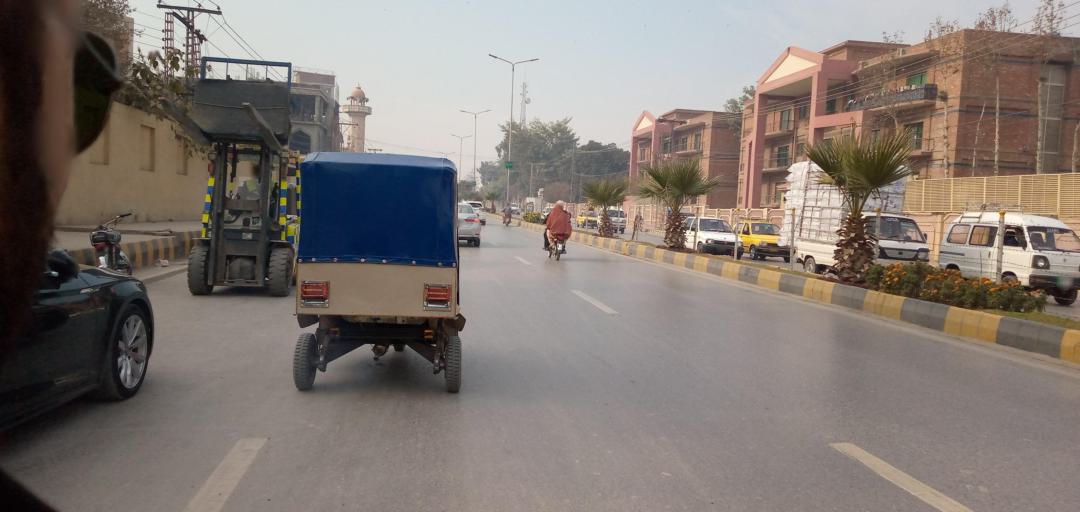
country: PK
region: Khyber Pakhtunkhwa
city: Peshawar
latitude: 34.0145
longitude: 71.5593
